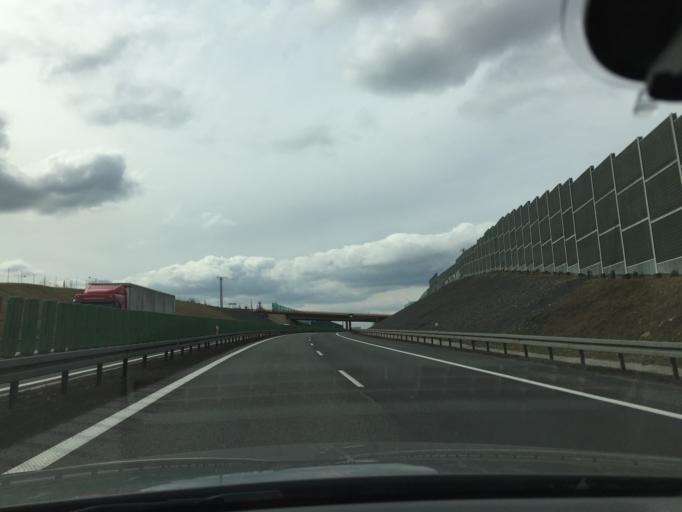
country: PL
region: Silesian Voivodeship
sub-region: Powiat cieszynski
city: Pogorze
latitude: 49.8009
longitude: 18.8462
